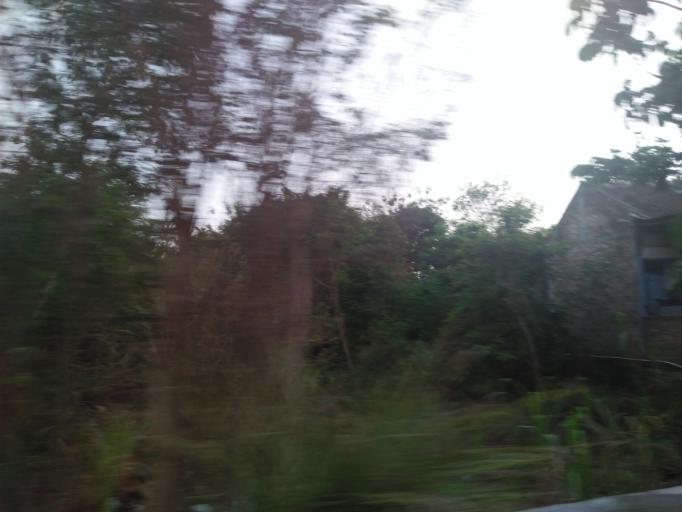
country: ID
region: Daerah Istimewa Yogyakarta
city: Sewon
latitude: -7.8442
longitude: 110.3980
